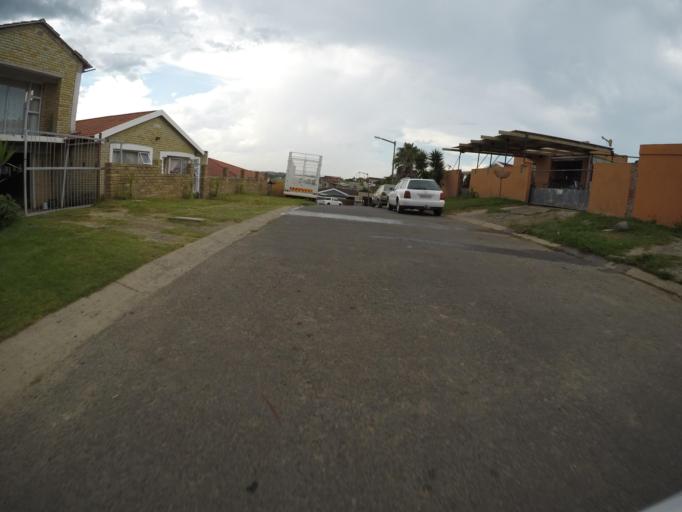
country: ZA
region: Eastern Cape
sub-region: Buffalo City Metropolitan Municipality
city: East London
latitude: -33.0222
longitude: 27.8656
